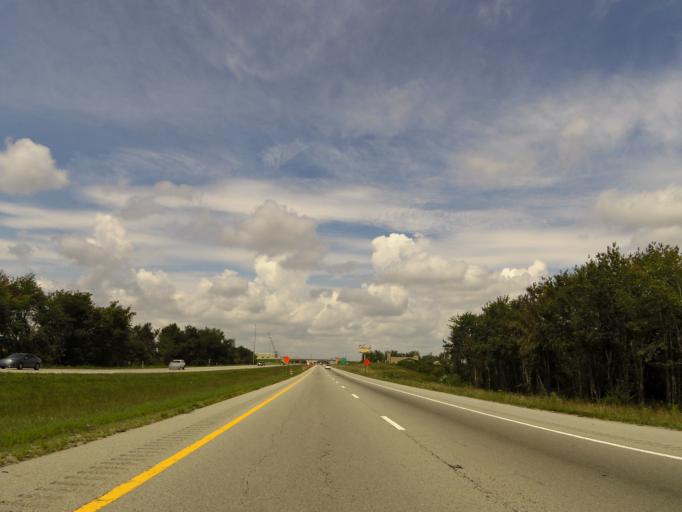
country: US
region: Tennessee
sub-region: Cumberland County
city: Crossville
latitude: 35.9787
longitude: -85.0073
